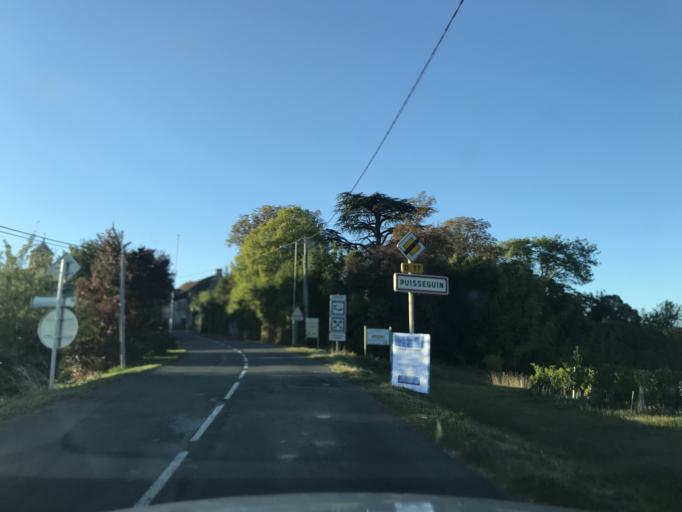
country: FR
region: Aquitaine
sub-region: Departement de la Gironde
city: Lussac
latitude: 44.9222
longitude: -0.0719
